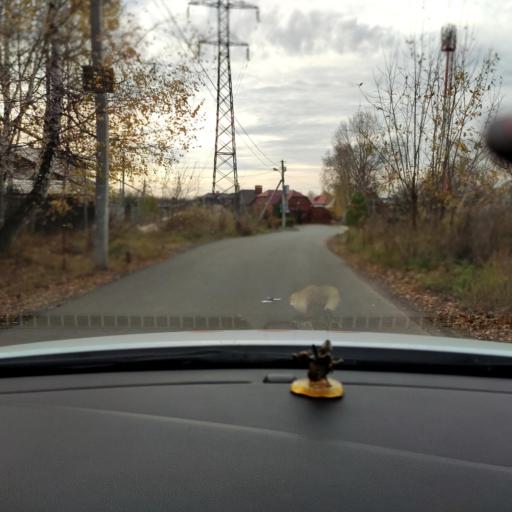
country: RU
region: Tatarstan
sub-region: Gorod Kazan'
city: Kazan
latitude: 55.7287
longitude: 49.1631
